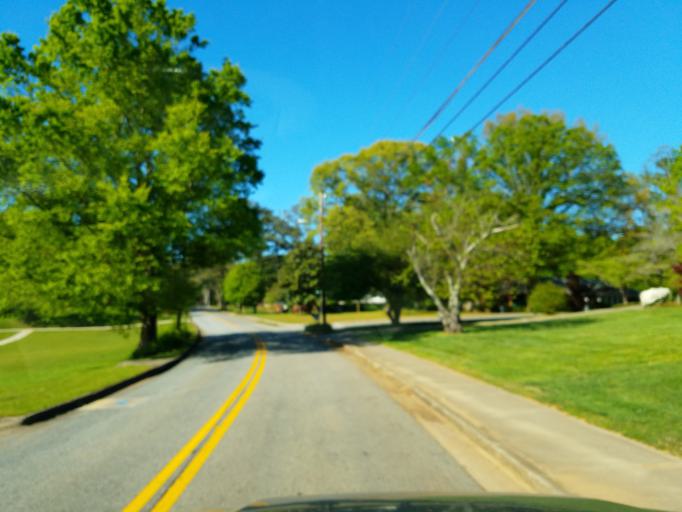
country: US
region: Georgia
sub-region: Cobb County
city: Smyrna
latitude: 33.8534
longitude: -84.5380
